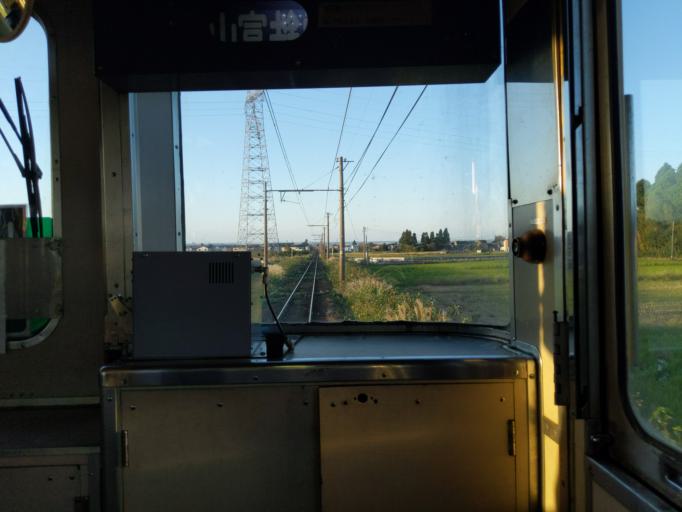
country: JP
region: Toyama
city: Kamiichi
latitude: 36.6488
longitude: 137.3179
